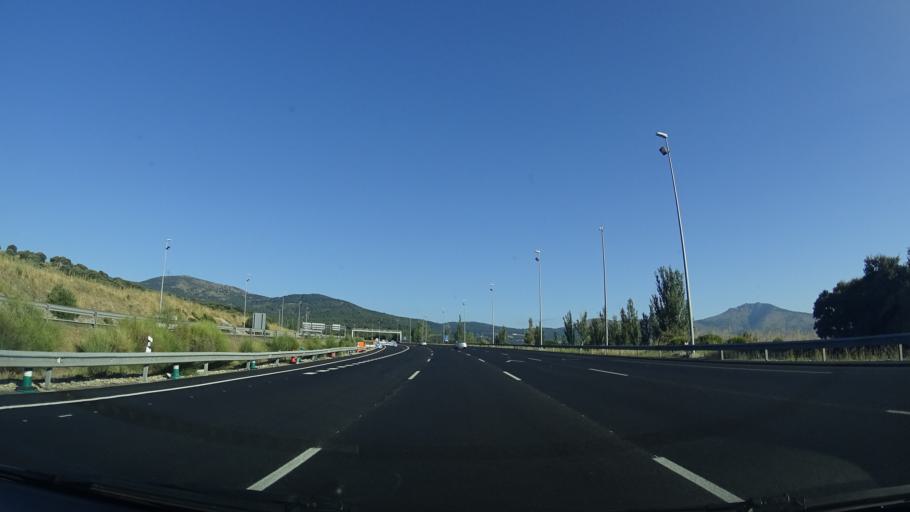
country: ES
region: Madrid
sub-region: Provincia de Madrid
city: Guadarrama
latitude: 40.6659
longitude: -4.1012
